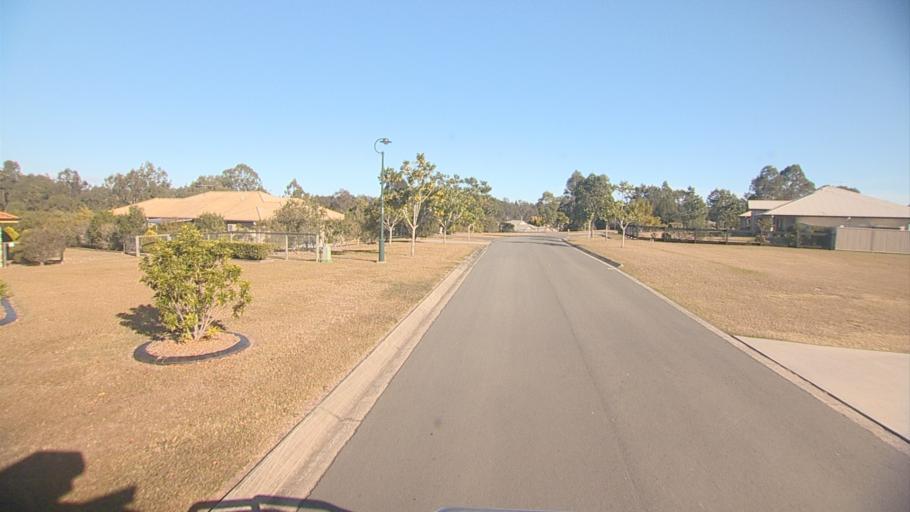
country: AU
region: Queensland
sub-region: Logan
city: North Maclean
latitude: -27.8292
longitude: 152.9981
